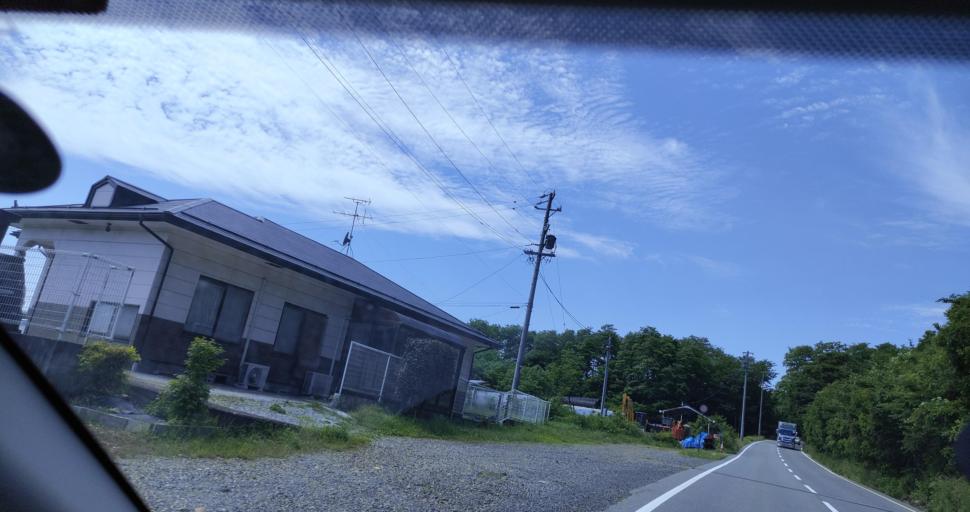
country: JP
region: Nagano
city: Ueda
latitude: 36.3835
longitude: 138.3289
